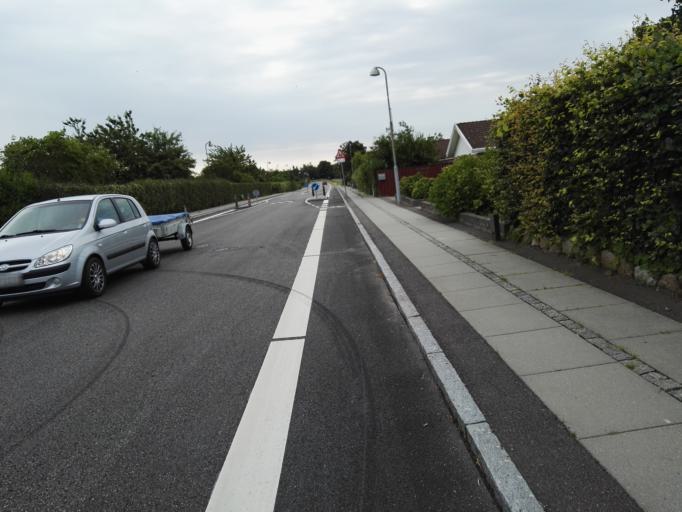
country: DK
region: Zealand
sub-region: Roskilde Kommune
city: Jyllinge
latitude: 55.7457
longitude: 12.1151
